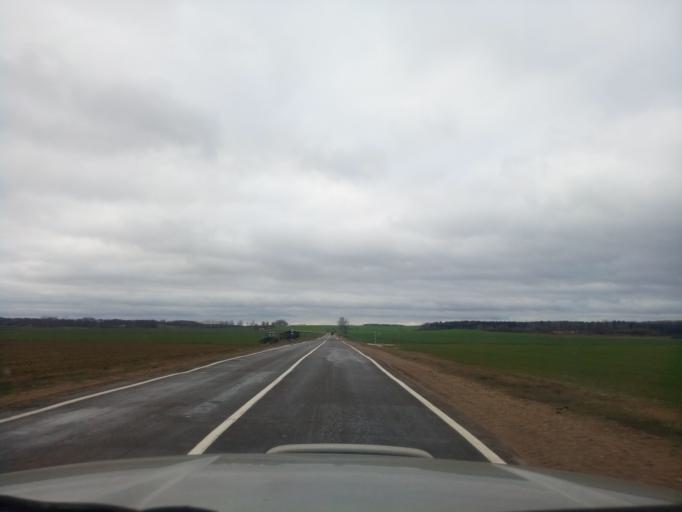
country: BY
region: Minsk
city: Kapyl'
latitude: 53.1928
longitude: 27.1922
